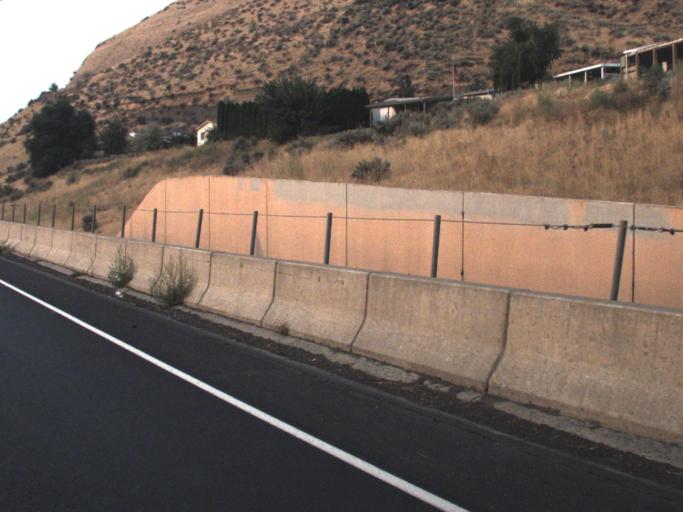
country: US
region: Washington
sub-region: Yakima County
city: Union Gap
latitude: 46.5363
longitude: -120.4745
